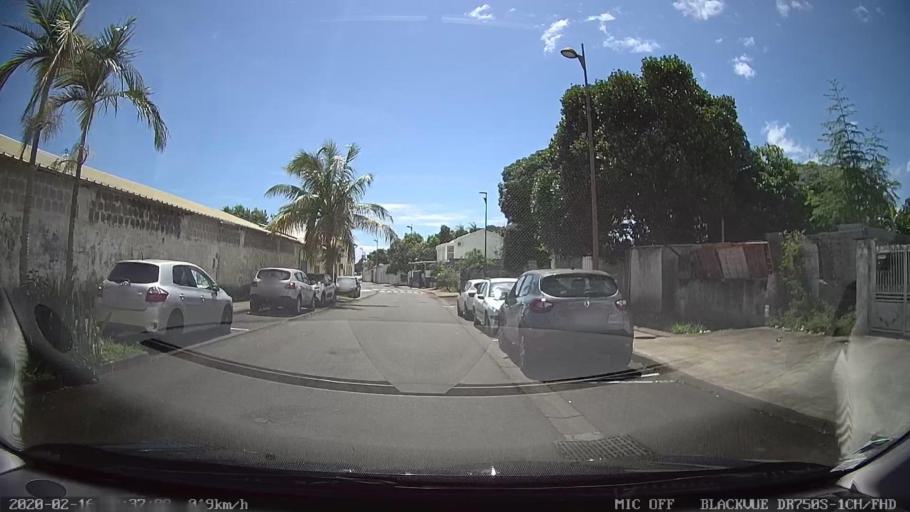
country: RE
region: Reunion
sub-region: Reunion
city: Saint-Denis
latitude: -20.8791
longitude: 55.4420
